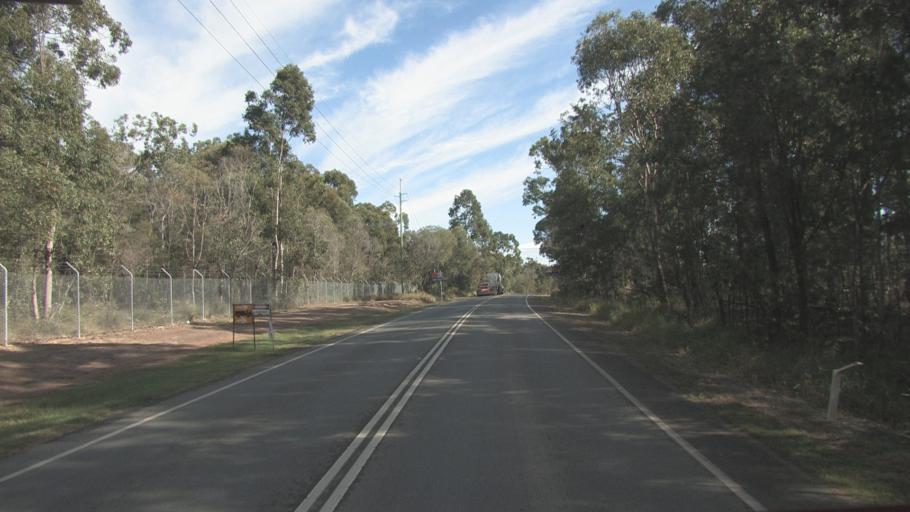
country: AU
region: Queensland
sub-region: Brisbane
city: Forest Lake
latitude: -27.6470
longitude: 152.9800
